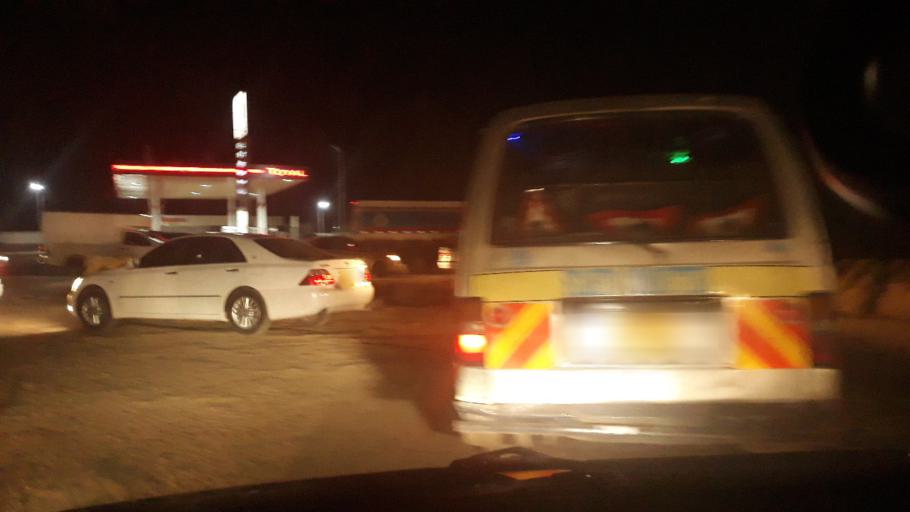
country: KE
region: Nairobi Area
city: Pumwani
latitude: -1.3131
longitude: 36.8549
